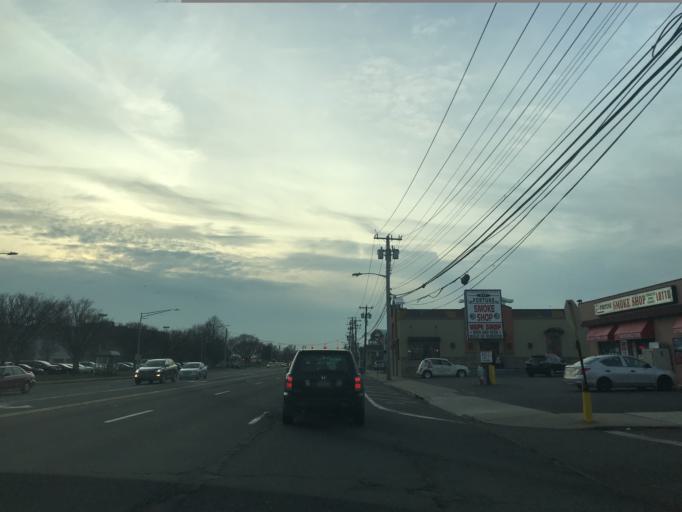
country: US
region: New York
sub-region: Nassau County
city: Westbury
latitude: 40.7471
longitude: -73.5937
